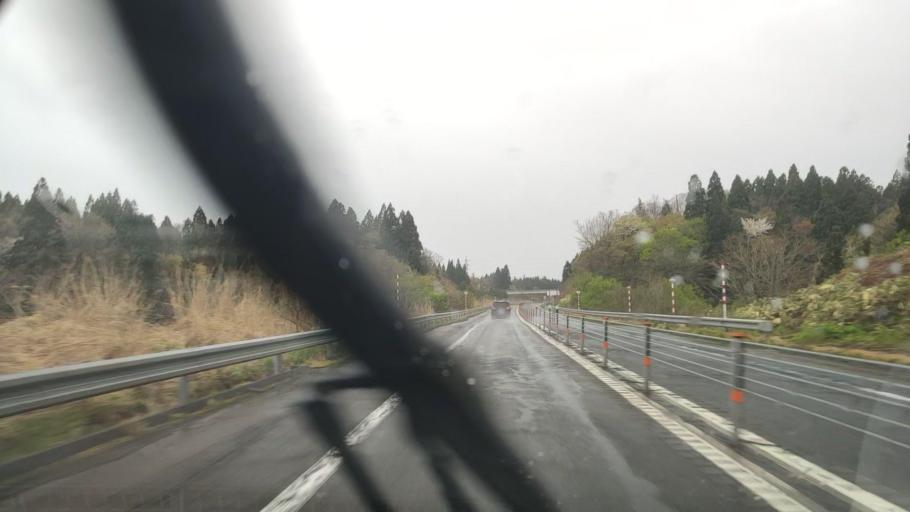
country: JP
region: Akita
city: Noshiromachi
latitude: 40.1706
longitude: 140.0527
